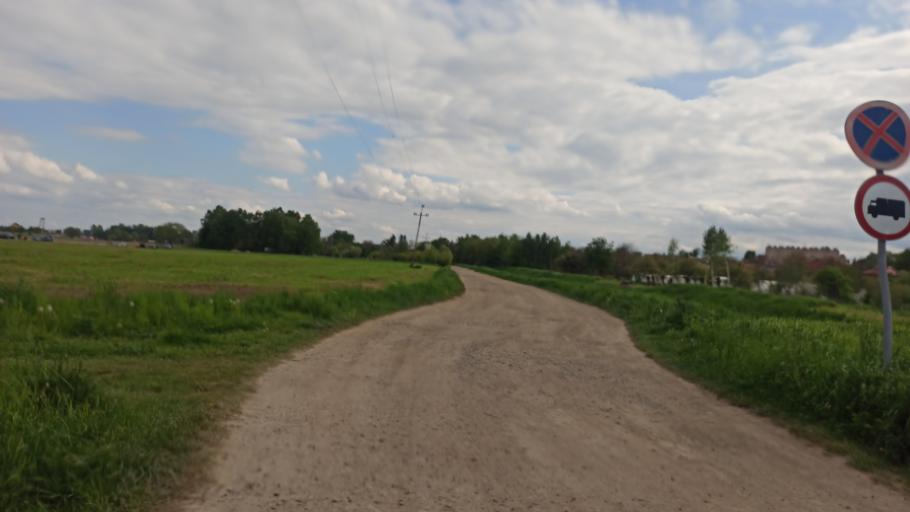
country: PL
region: Subcarpathian Voivodeship
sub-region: Powiat jaroslawski
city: Radymno
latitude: 49.9555
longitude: 22.8224
